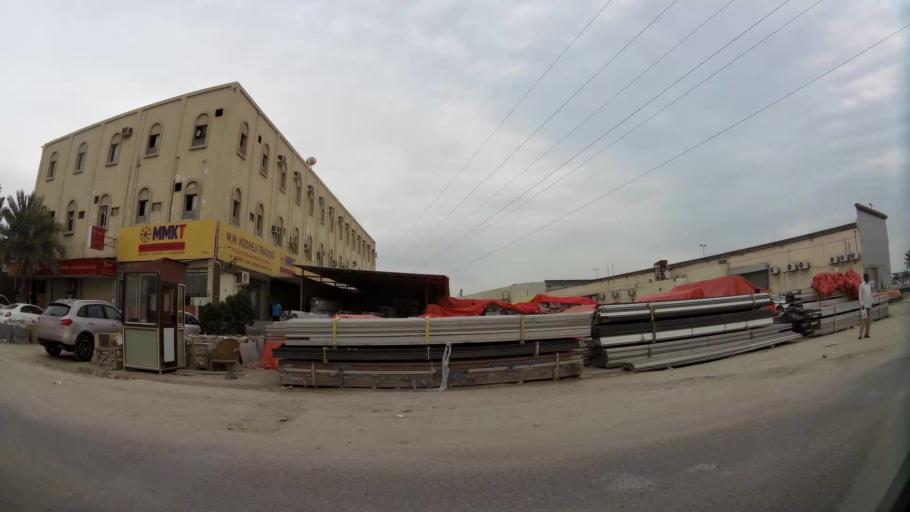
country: BH
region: Northern
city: Sitrah
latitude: 26.1368
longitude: 50.6066
